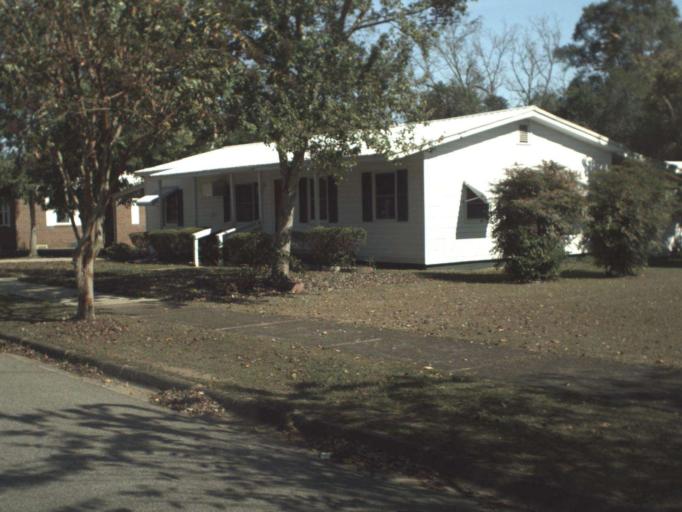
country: US
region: Florida
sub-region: Gadsden County
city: Gretna
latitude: 30.5669
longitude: -84.7438
